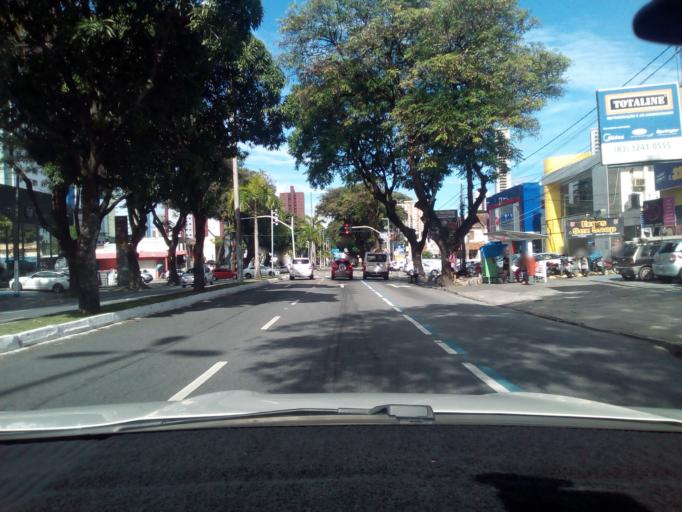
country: BR
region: Paraiba
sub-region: Joao Pessoa
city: Joao Pessoa
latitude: -7.1196
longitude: -34.8397
